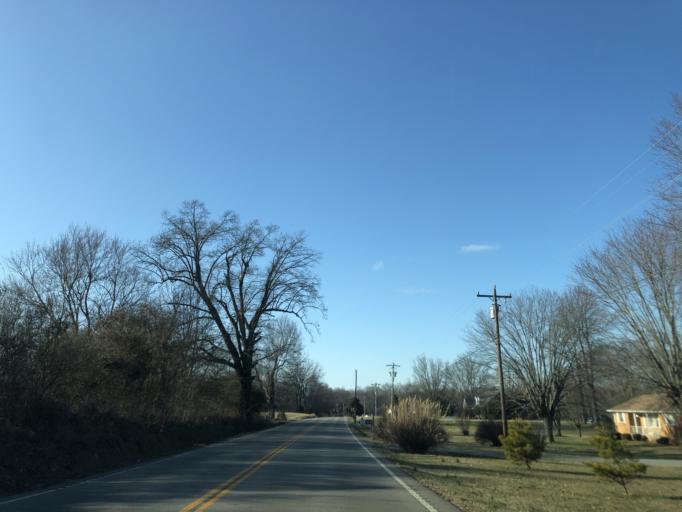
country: US
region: Tennessee
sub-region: Sumner County
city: White House
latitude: 36.4922
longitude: -86.5896
